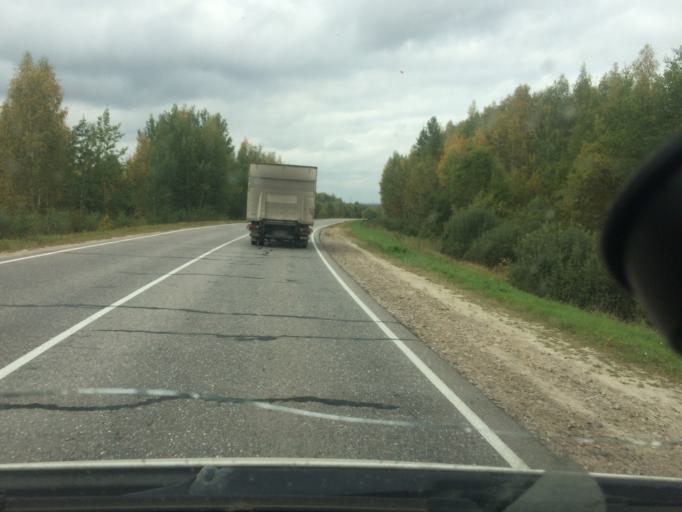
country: RU
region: Tula
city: Suvorov
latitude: 54.0761
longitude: 36.5469
